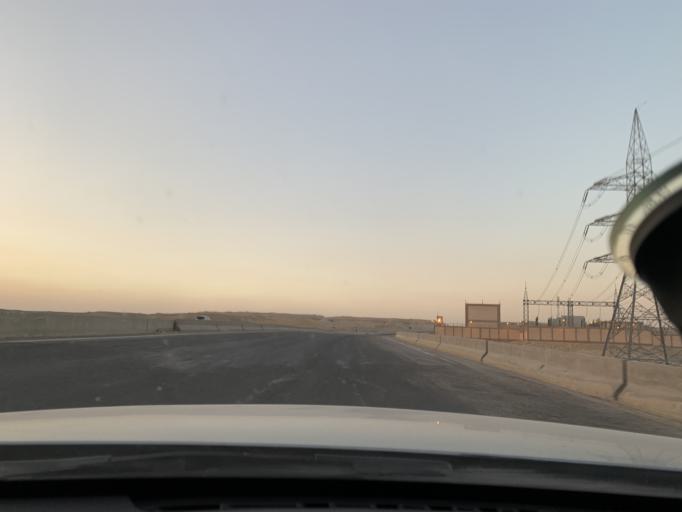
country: EG
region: Muhafazat al Qahirah
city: Halwan
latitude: 29.9364
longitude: 31.5289
